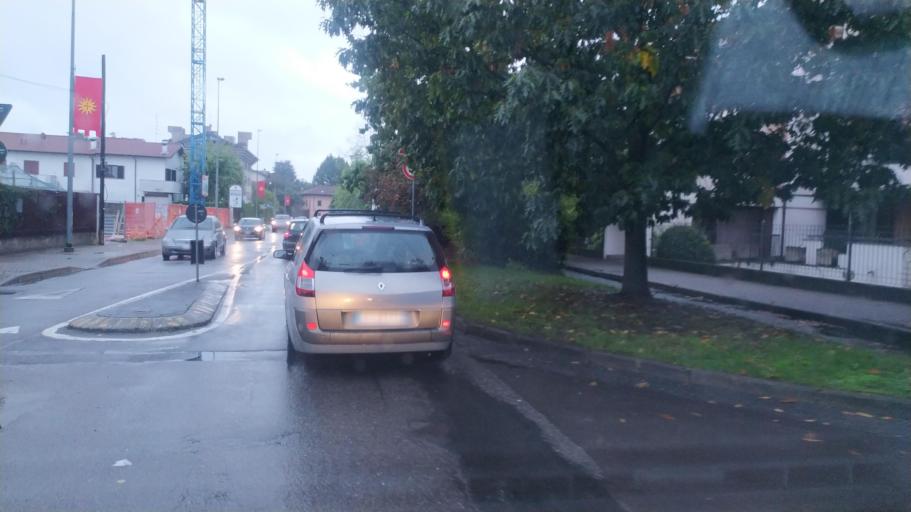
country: IT
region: Lombardy
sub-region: Citta metropolitana di Milano
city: Legnano
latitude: 45.6052
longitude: 8.9294
